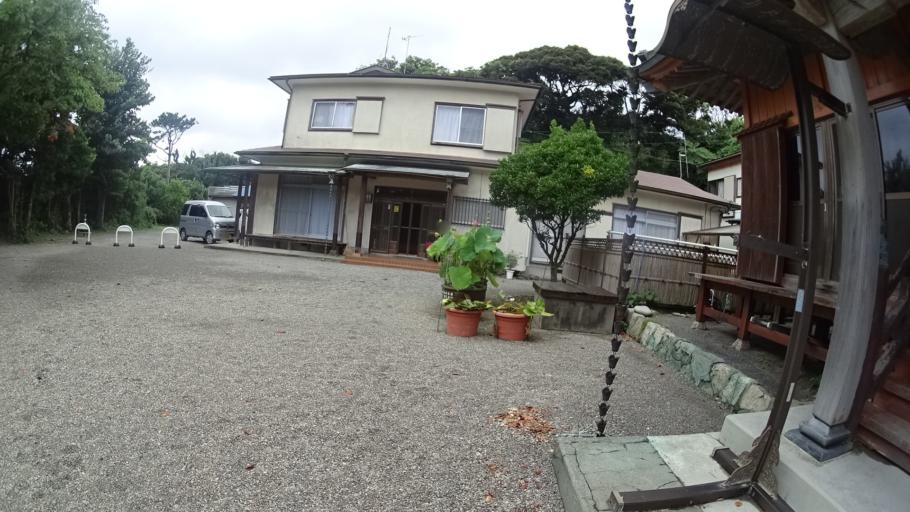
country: JP
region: Shizuoka
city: Shimoda
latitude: 34.3246
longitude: 139.2210
